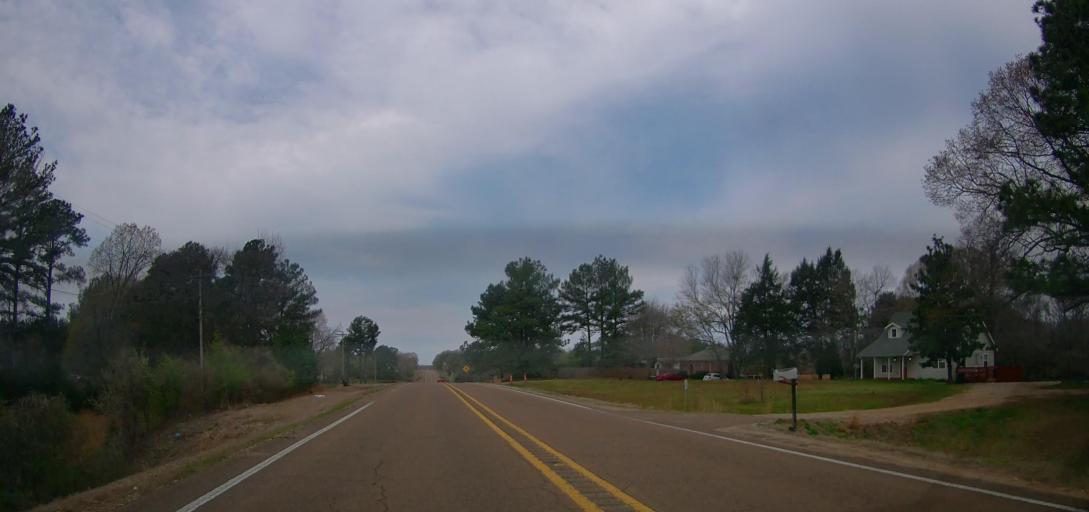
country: US
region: Mississippi
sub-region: Marshall County
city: Byhalia
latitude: 34.8402
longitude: -89.6003
